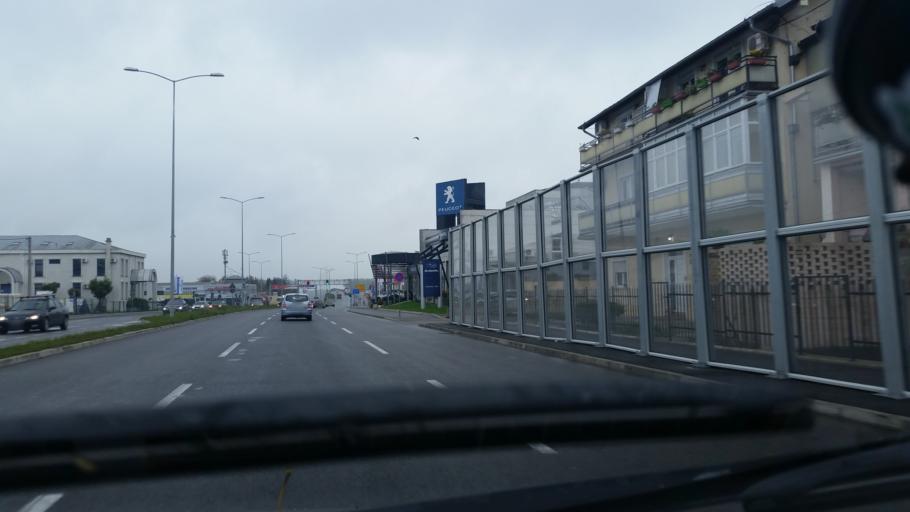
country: RS
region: Central Serbia
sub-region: Belgrade
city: Zemun
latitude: 44.8581
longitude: 20.3754
